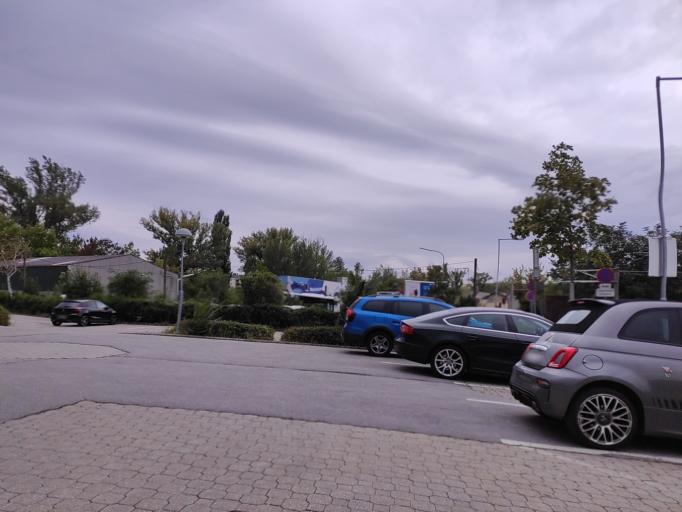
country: AT
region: Lower Austria
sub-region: Politischer Bezirk Baden
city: Pfaffstatten
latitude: 47.9985
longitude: 16.2554
